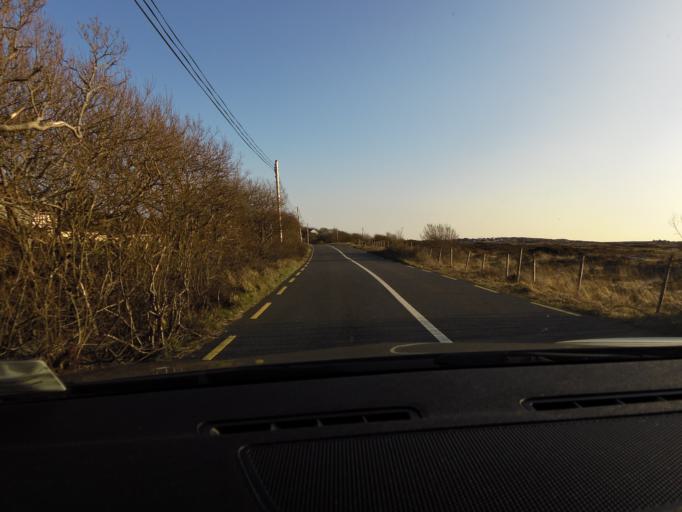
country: IE
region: Connaught
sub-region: County Galway
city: Oughterard
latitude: 53.3092
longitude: -9.5553
